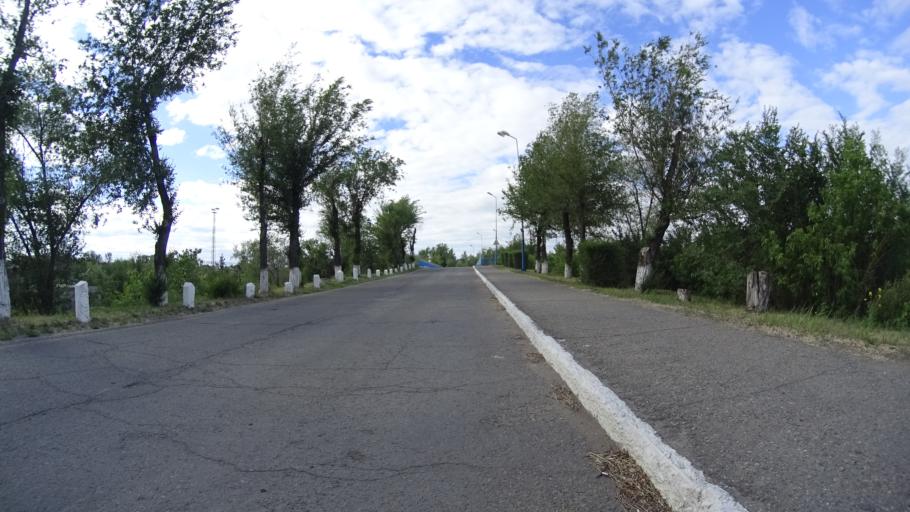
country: RU
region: Chelyabinsk
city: Troitsk
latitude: 54.0389
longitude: 61.6398
